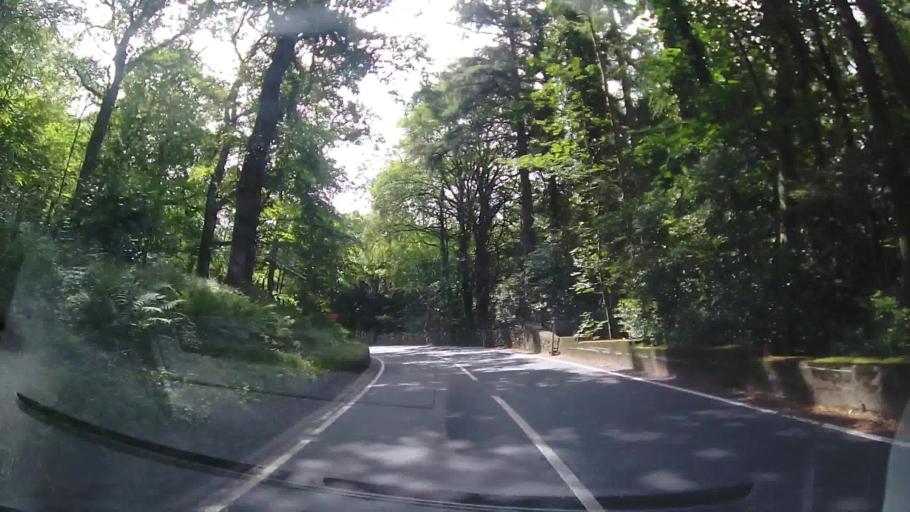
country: GB
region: Wales
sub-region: Denbighshire
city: Corwen
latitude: 52.9759
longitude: -3.3869
